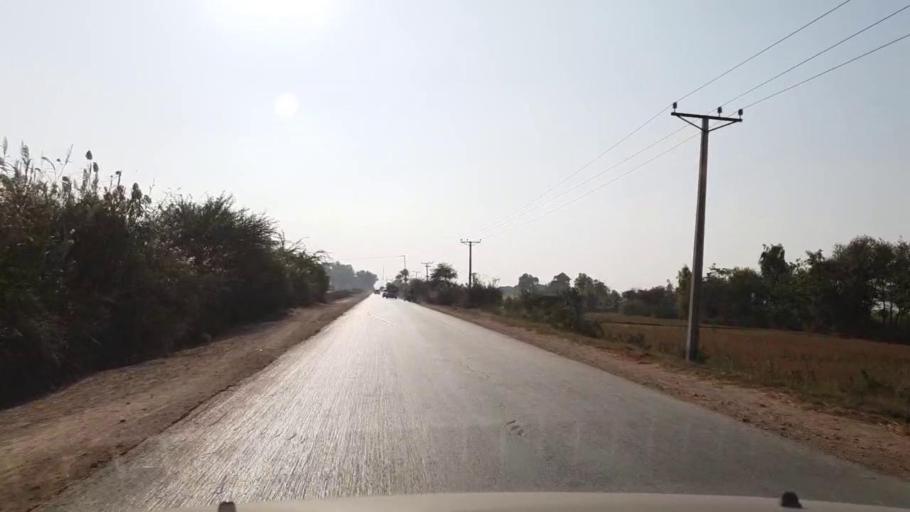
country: PK
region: Sindh
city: Tando Muhammad Khan
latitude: 25.0602
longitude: 68.4619
